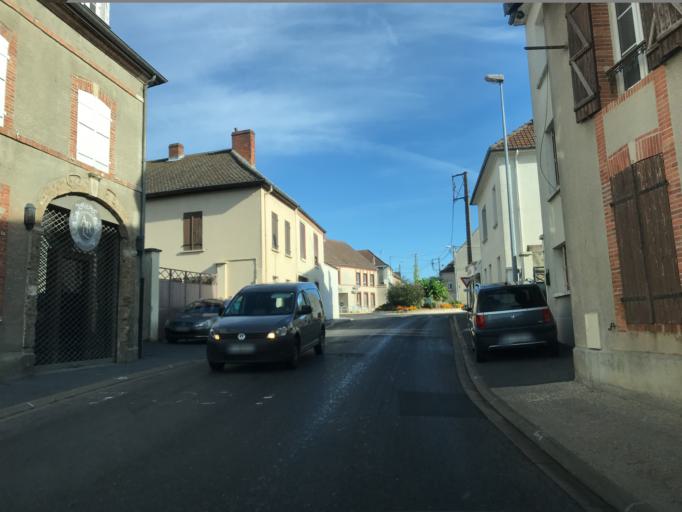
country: FR
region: Champagne-Ardenne
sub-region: Departement de la Marne
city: Damery
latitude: 49.0719
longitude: 3.8780
